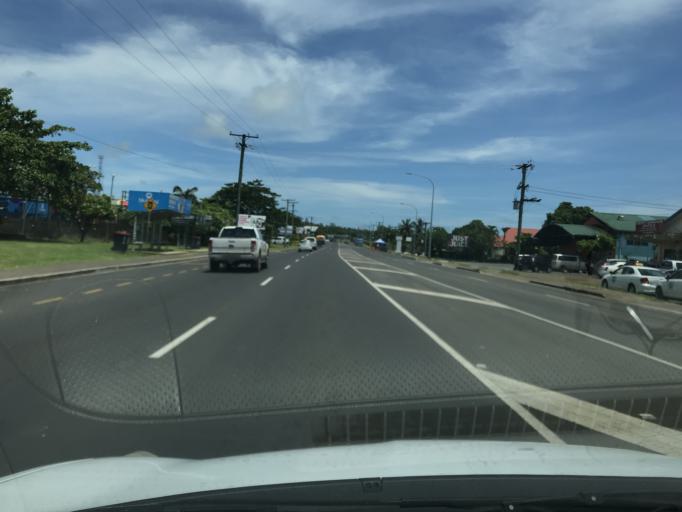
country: WS
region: Tuamasaga
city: Vaiusu
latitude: -13.8212
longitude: -171.8026
